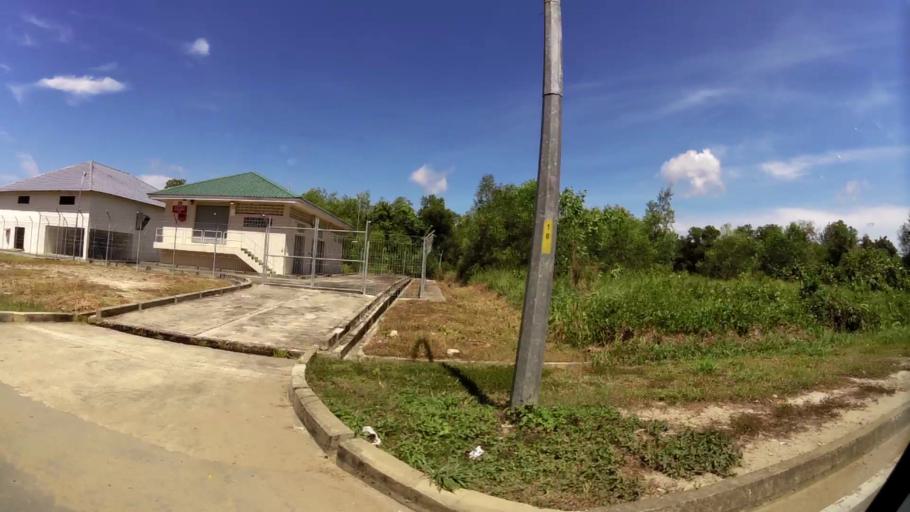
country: BN
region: Brunei and Muara
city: Bandar Seri Begawan
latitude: 4.9414
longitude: 114.9385
